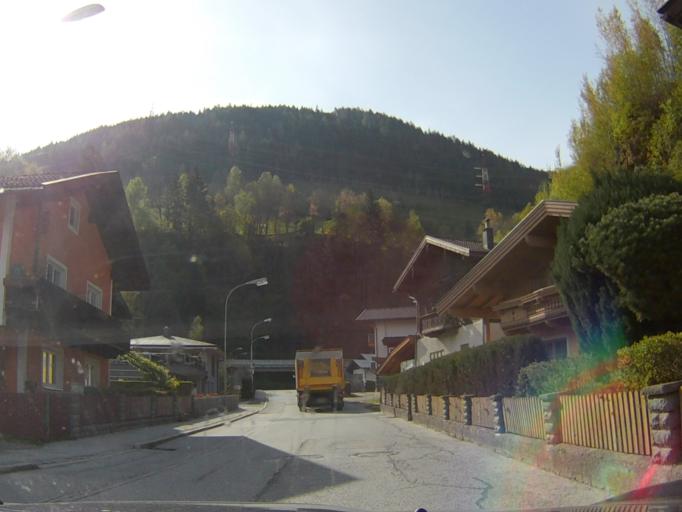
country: AT
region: Salzburg
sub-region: Politischer Bezirk Zell am See
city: Mittersill
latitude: 47.2742
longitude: 12.4844
